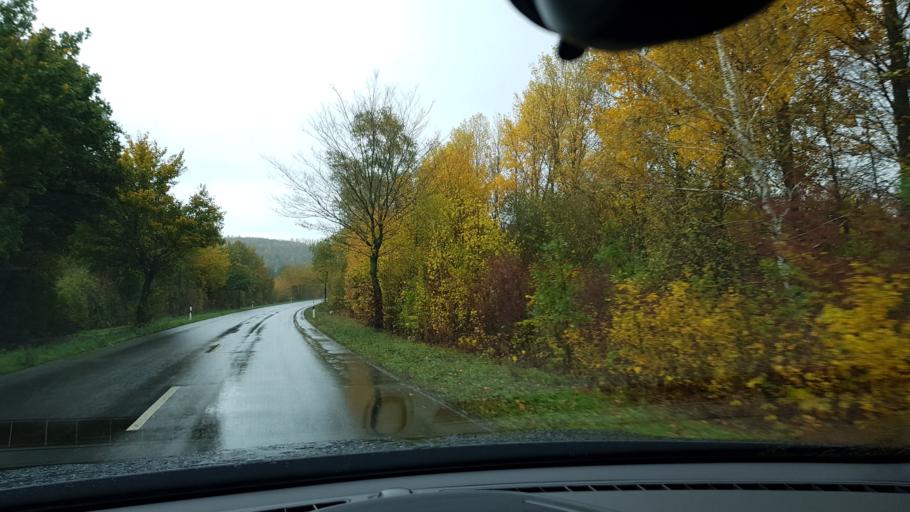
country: DE
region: North Rhine-Westphalia
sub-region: Regierungsbezirk Dusseldorf
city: Grevenbroich
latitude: 51.0438
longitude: 6.5865
